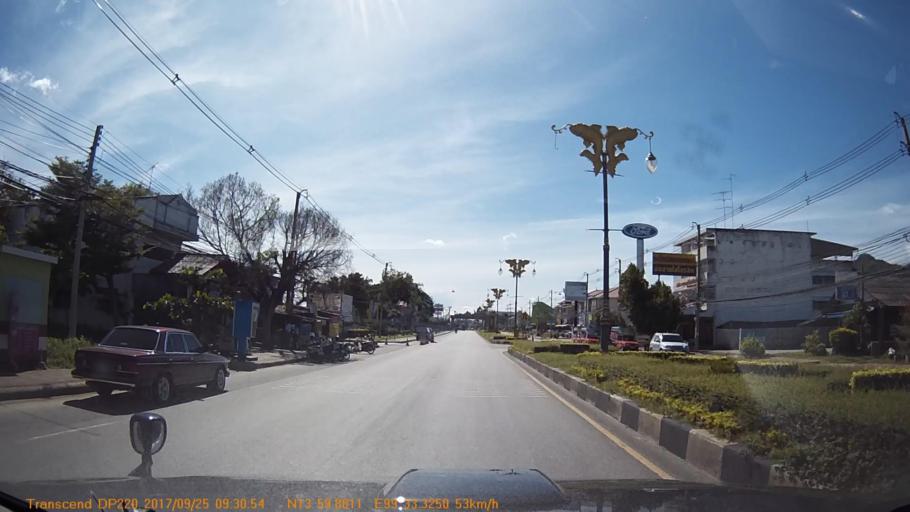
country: TH
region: Kanchanaburi
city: Kanchanaburi
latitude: 13.9979
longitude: 99.5556
